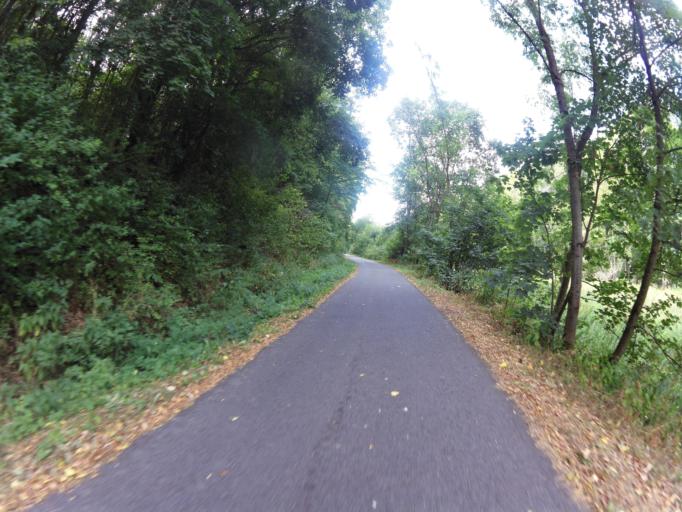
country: DE
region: Bavaria
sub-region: Regierungsbezirk Unterfranken
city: Gaukonigshofen
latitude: 49.6502
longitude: 10.0198
